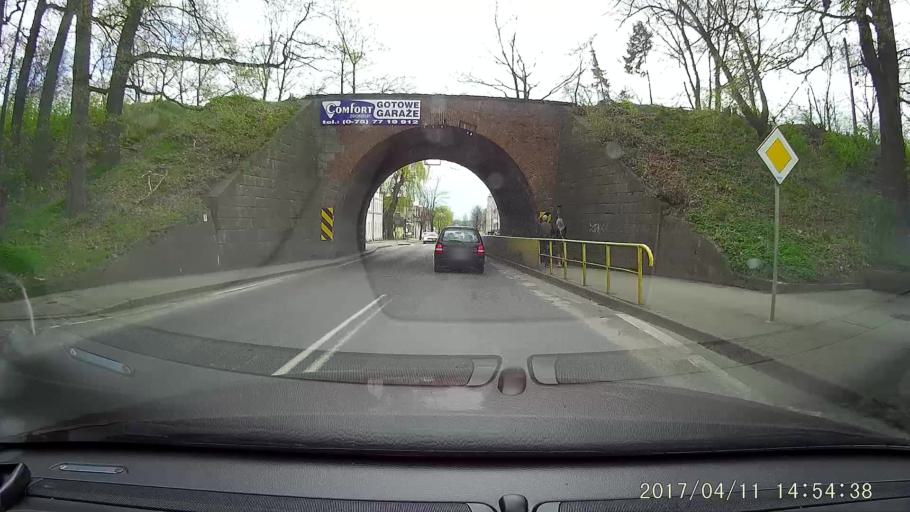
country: PL
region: Lower Silesian Voivodeship
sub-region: Powiat zgorzelecki
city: Zgorzelec
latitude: 51.1416
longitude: 15.0110
